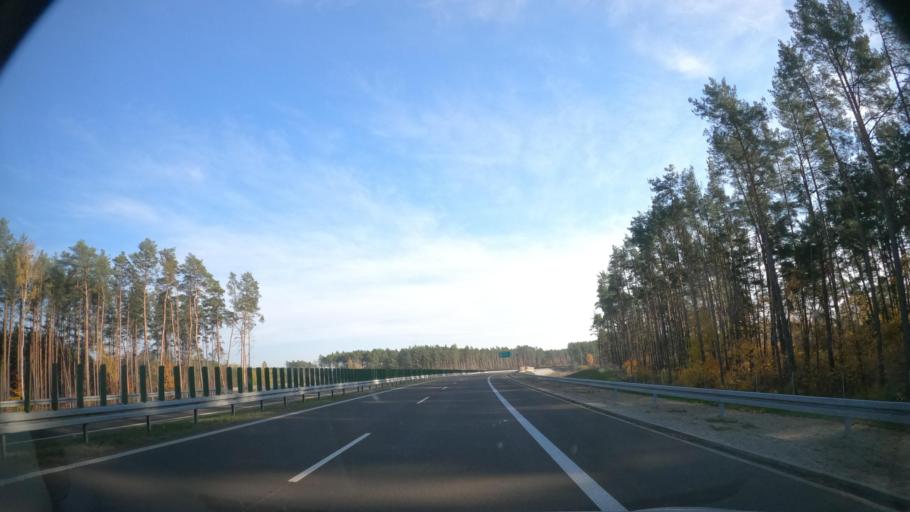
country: PL
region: West Pomeranian Voivodeship
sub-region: Powiat walecki
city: Walcz
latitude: 53.2931
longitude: 16.4968
